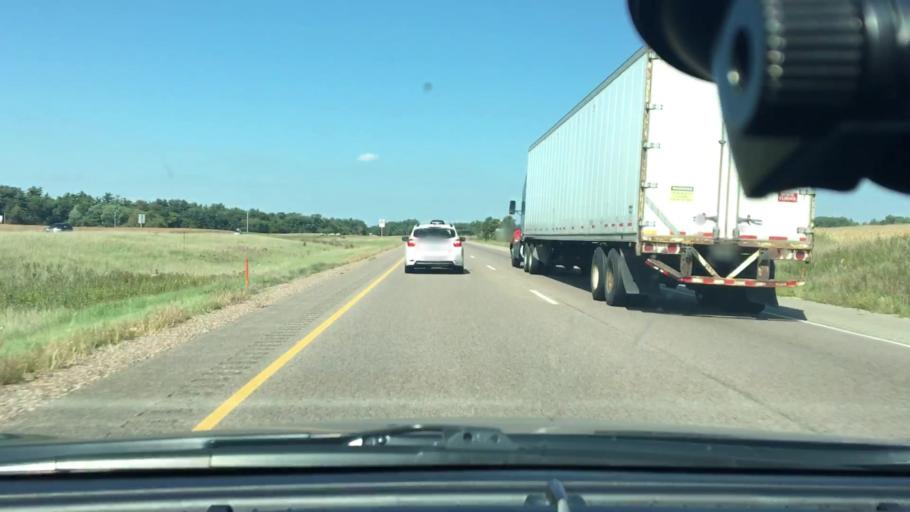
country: US
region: Wisconsin
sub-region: Eau Claire County
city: Altoona
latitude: 44.7391
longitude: -91.3730
